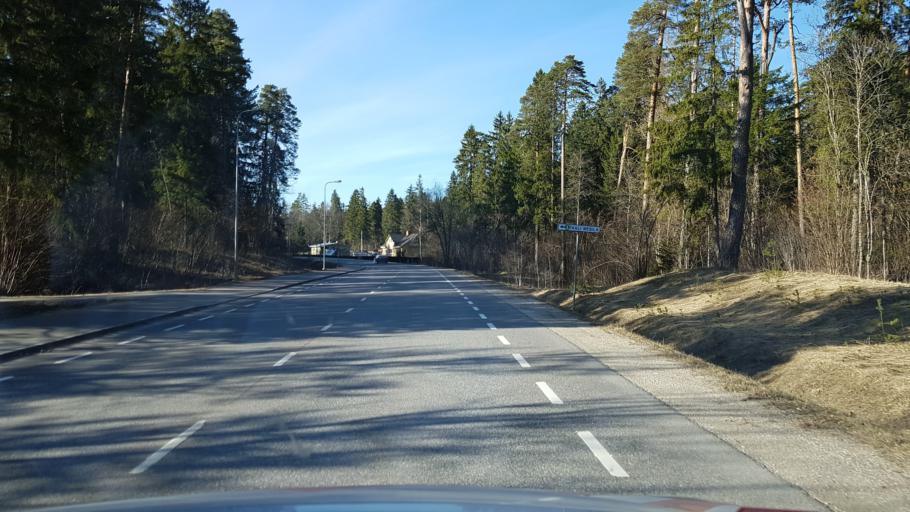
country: EE
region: Laeaene-Virumaa
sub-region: Vinni vald
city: Vinni
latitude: 59.1691
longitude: 26.5858
